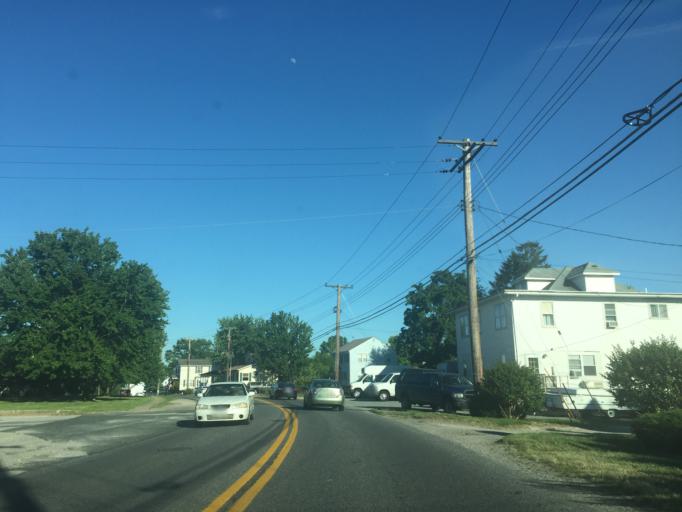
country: US
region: Maryland
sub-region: Baltimore County
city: Parkville
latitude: 39.3814
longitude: -76.5322
